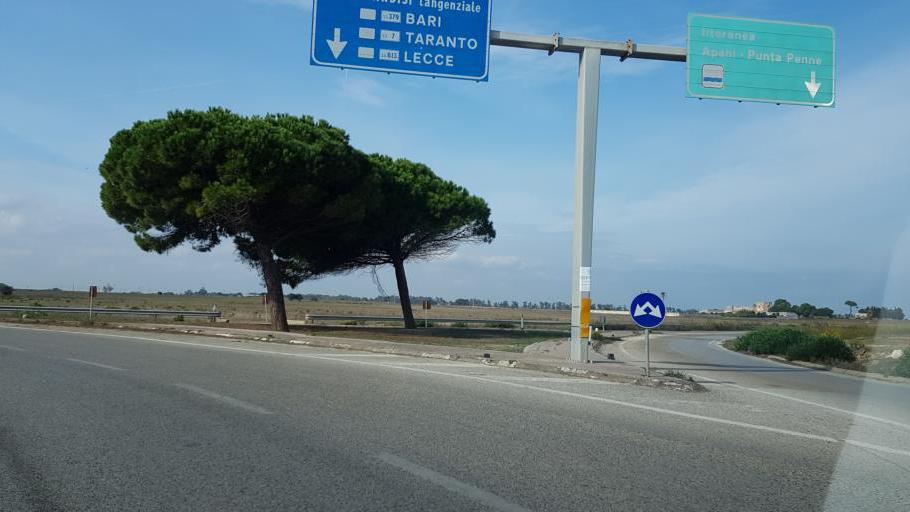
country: IT
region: Apulia
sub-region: Provincia di Brindisi
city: Brindisi
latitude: 40.6656
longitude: 17.9204
